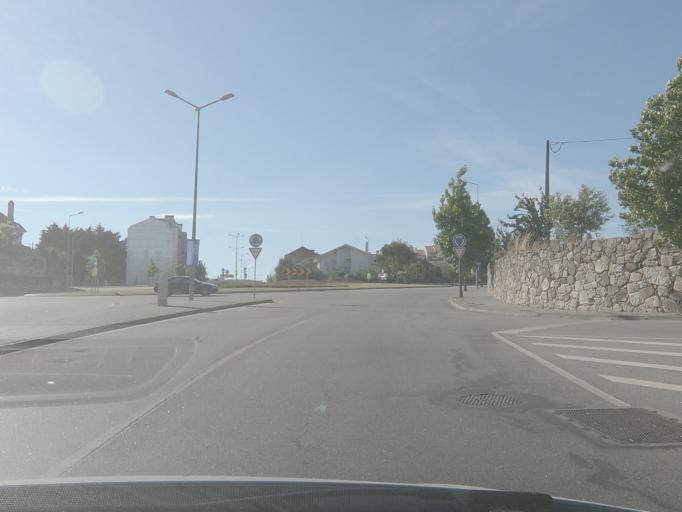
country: PT
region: Viseu
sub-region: Viseu
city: Abraveses
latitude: 40.6755
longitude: -7.9233
